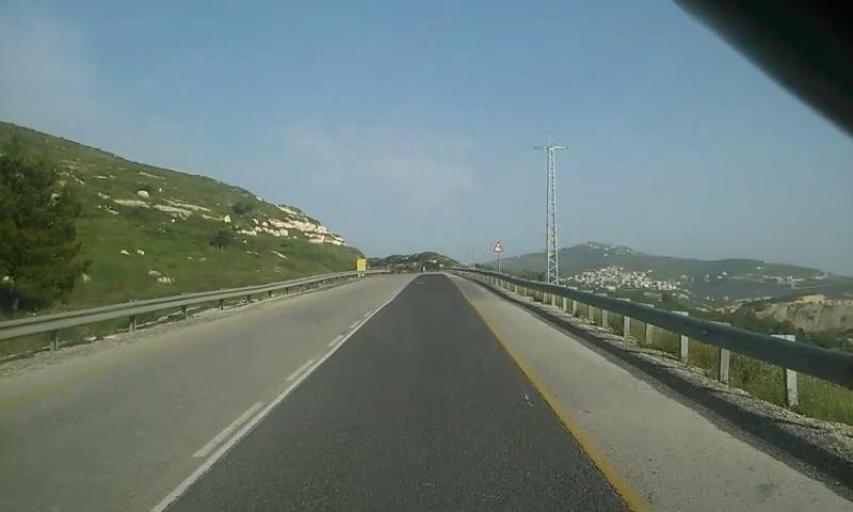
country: PS
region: West Bank
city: Sarrah
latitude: 32.1916
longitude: 35.1947
